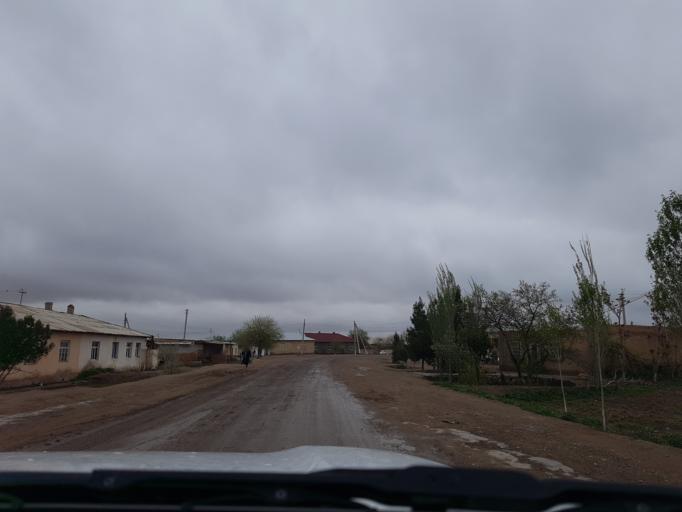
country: TM
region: Lebap
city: Sayat
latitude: 38.4566
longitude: 64.3791
